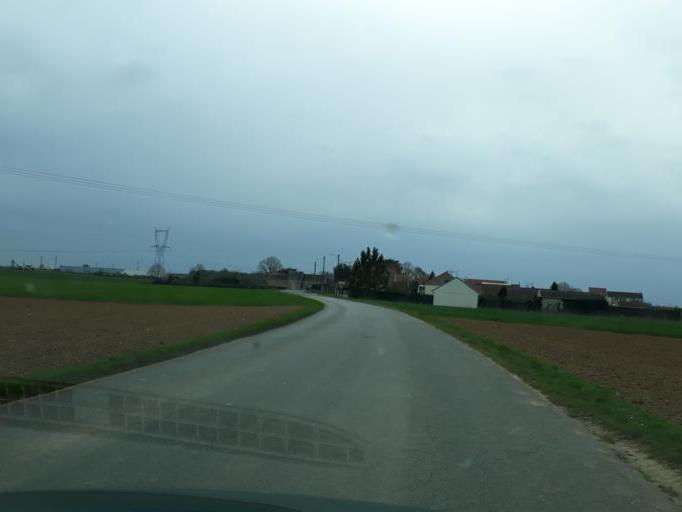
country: FR
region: Centre
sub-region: Departement du Loir-et-Cher
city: Villebarou
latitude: 47.6434
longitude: 1.3003
